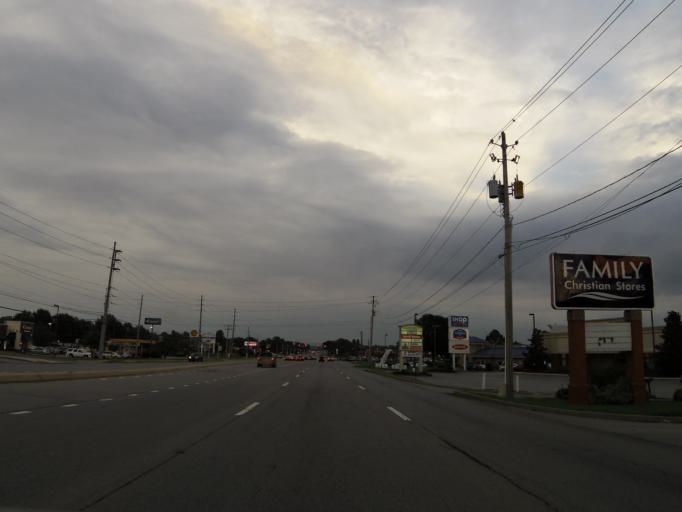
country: US
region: Alabama
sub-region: Madison County
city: Redstone Arsenal
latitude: 34.7447
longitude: -86.6801
